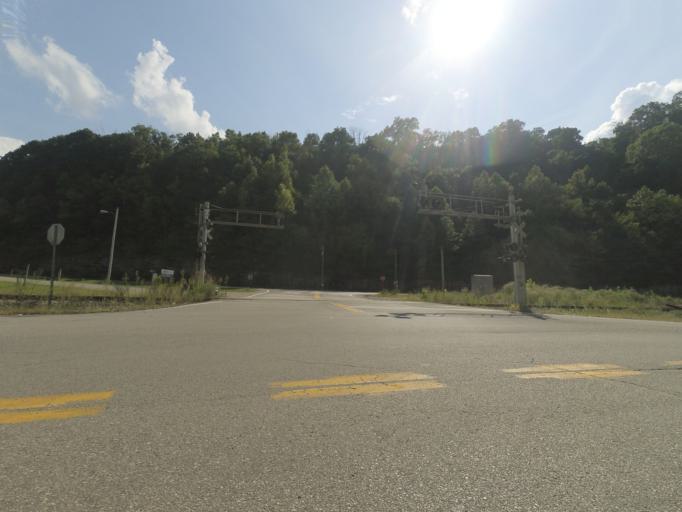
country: US
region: West Virginia
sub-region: Wayne County
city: Ceredo
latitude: 38.3769
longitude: -82.5587
